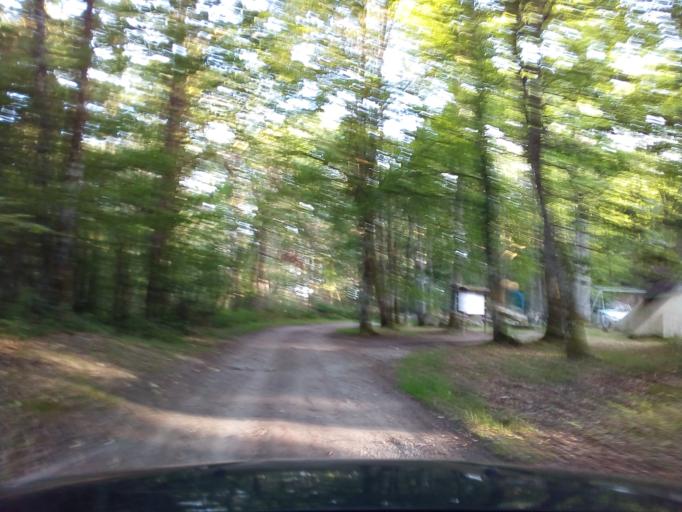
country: FR
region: Limousin
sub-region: Departement de la Creuse
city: Gouzon
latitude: 46.1084
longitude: 2.1636
